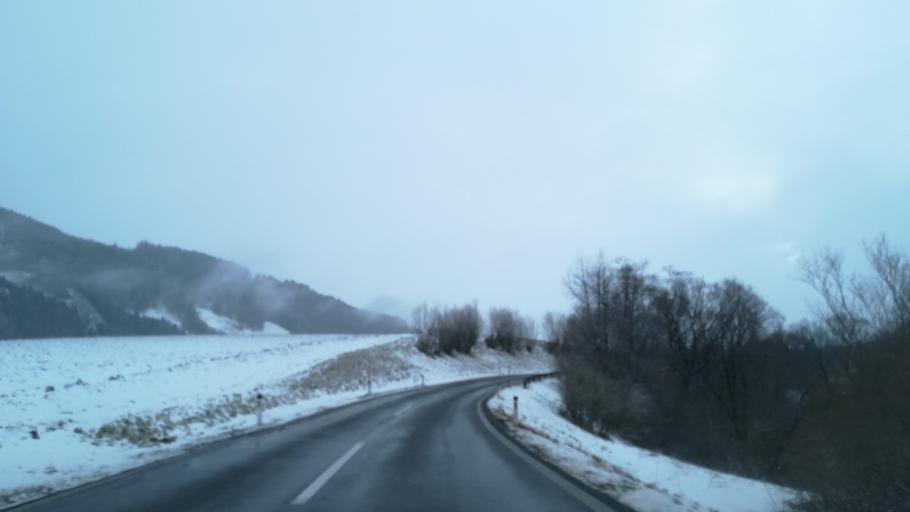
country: AT
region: Styria
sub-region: Politischer Bezirk Murtal
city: Poels
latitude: 47.2199
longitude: 14.6028
